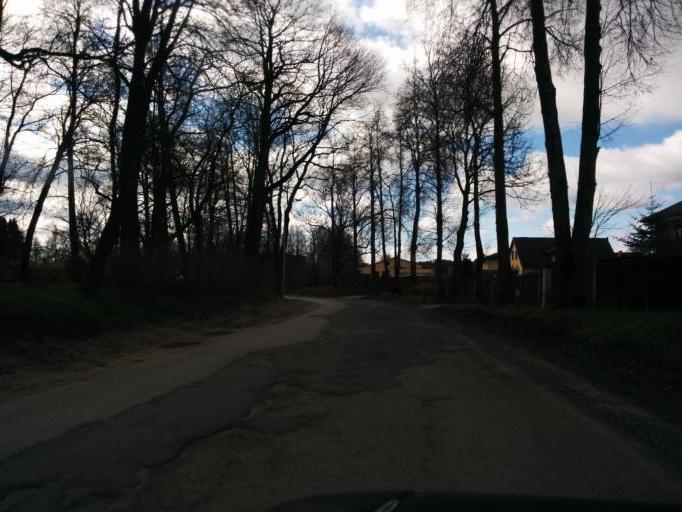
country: LV
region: Kekava
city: Balozi
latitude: 56.8891
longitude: 24.1564
